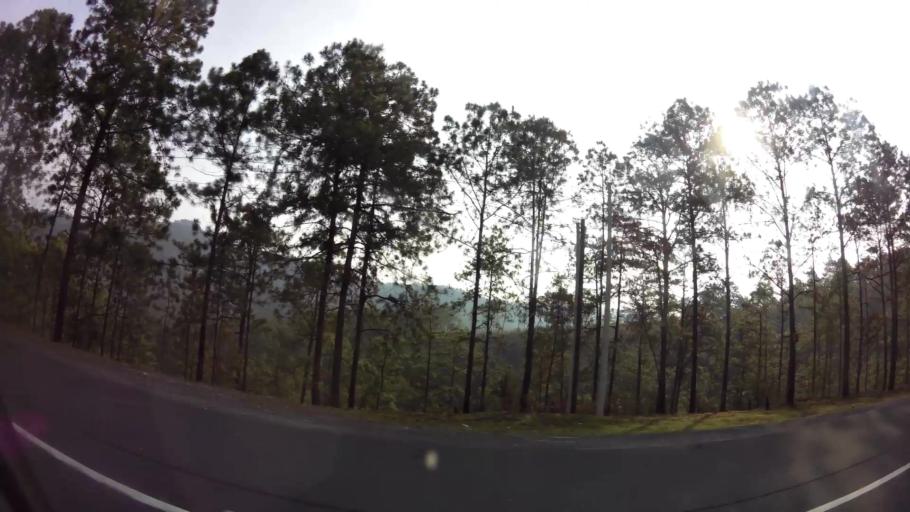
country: HN
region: Francisco Morazan
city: Zambrano
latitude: 14.2847
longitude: -87.4677
